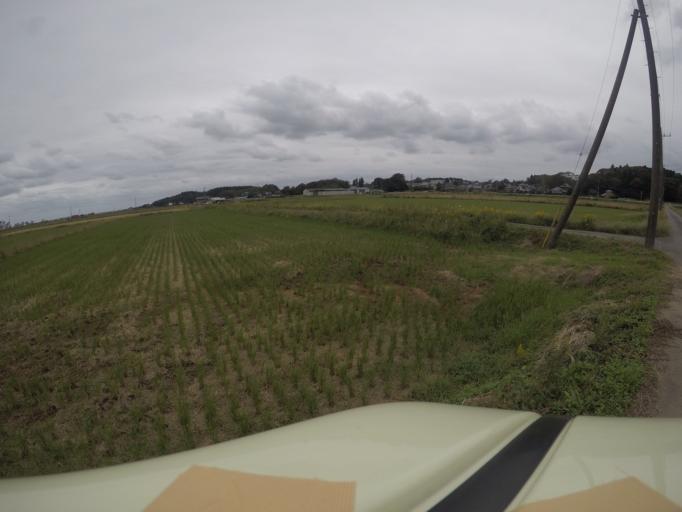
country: JP
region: Ibaraki
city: Ami
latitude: 36.0353
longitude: 140.2534
